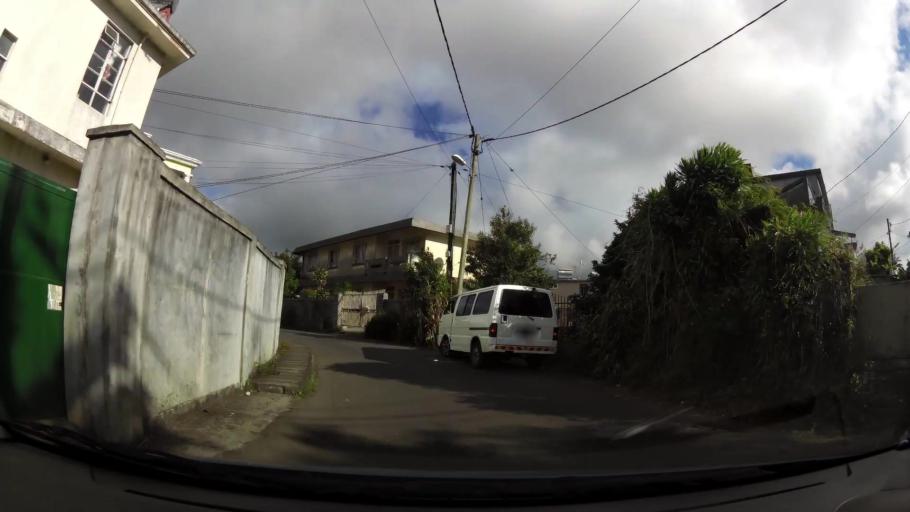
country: MU
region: Plaines Wilhems
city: Curepipe
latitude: -20.3262
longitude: 57.5182
